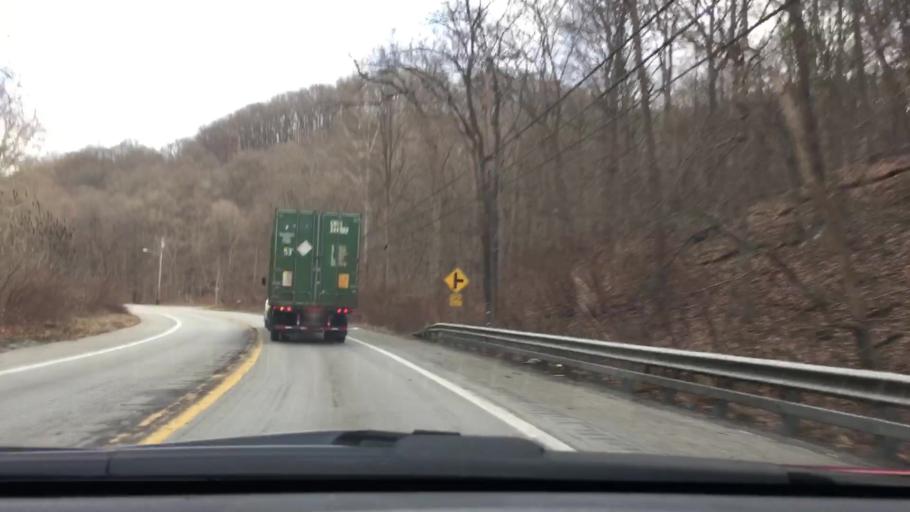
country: US
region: Pennsylvania
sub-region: Allegheny County
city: Pitcairn
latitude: 40.4038
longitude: -79.7632
